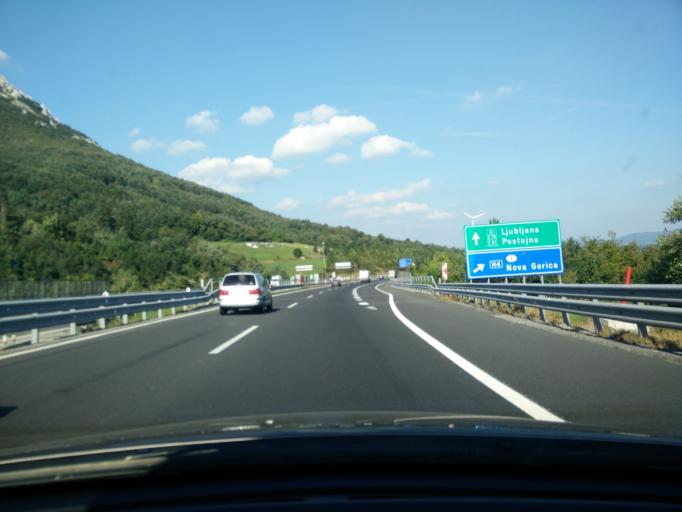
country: SI
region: Divaca
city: Divaca
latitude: 45.7570
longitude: 14.0536
